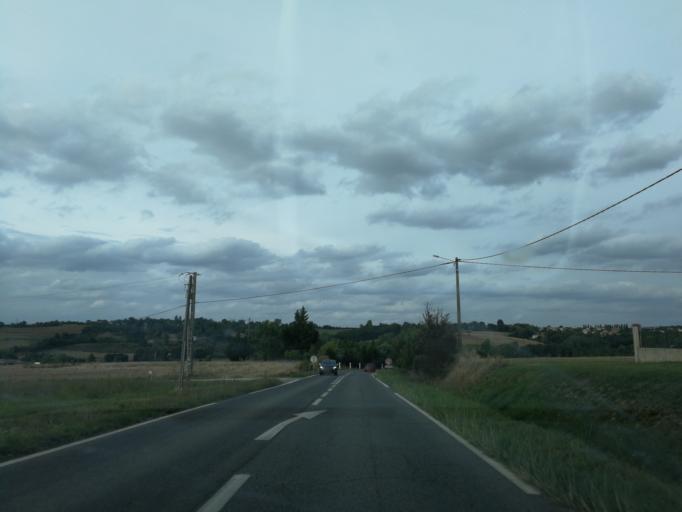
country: FR
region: Midi-Pyrenees
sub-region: Departement de la Haute-Garonne
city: Dremil-Lafage
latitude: 43.5914
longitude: 1.5874
